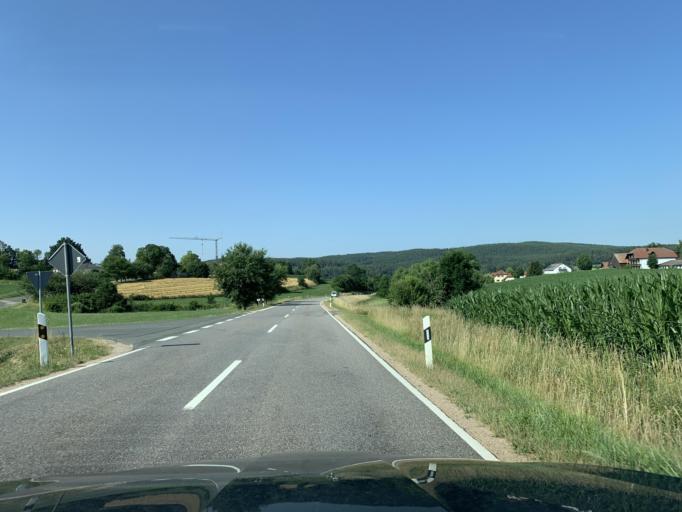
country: DE
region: Bavaria
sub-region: Upper Palatinate
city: Schwarzhofen
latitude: 49.3828
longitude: 12.3486
